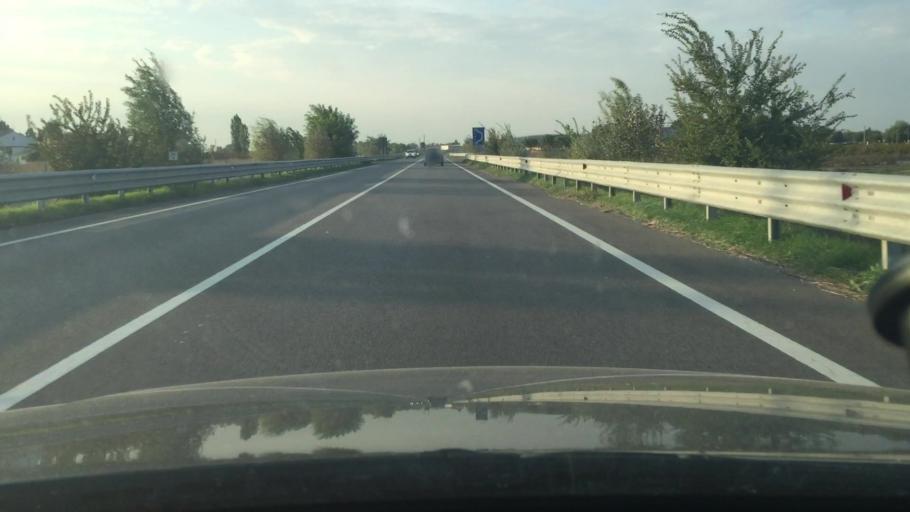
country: IT
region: Emilia-Romagna
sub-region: Provincia di Ferrara
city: Porotto-Cassama
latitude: 44.8350
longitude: 11.5759
